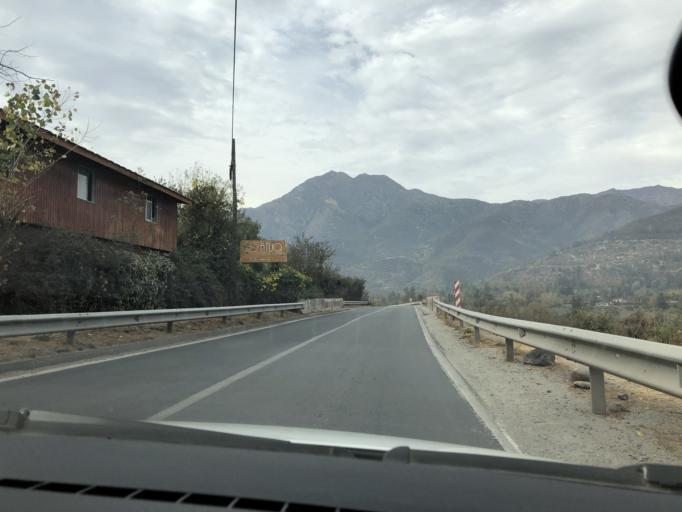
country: CL
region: Santiago Metropolitan
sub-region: Provincia de Cordillera
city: Puente Alto
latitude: -33.5980
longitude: -70.4992
